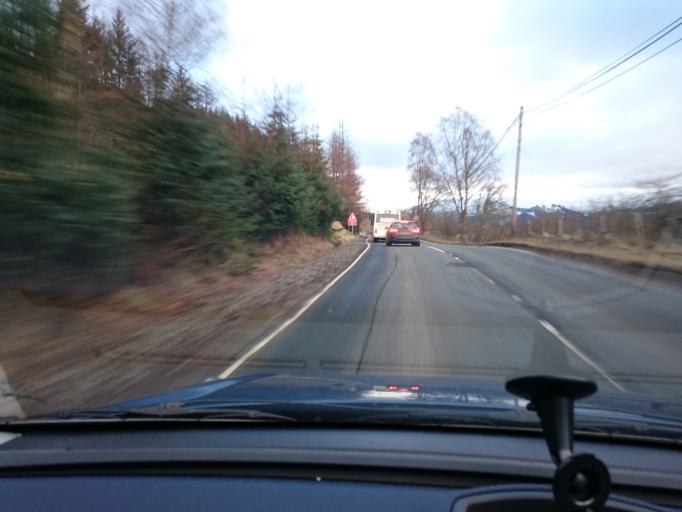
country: GB
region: Scotland
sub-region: Stirling
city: Callander
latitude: 56.3424
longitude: -4.3264
